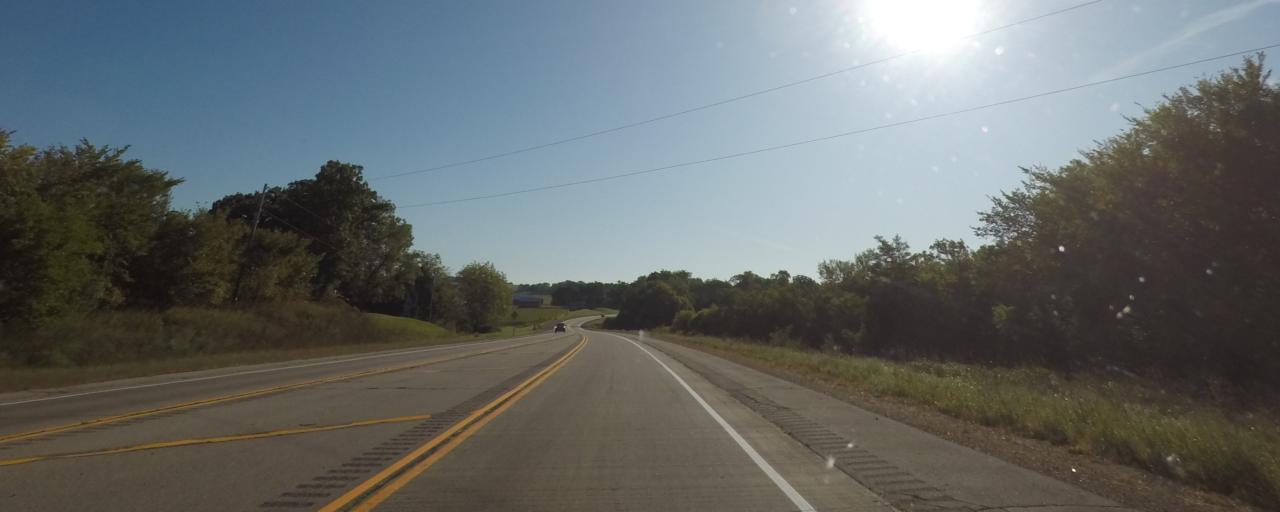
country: US
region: Wisconsin
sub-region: Dane County
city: Cottage Grove
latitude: 43.0286
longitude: -89.1812
